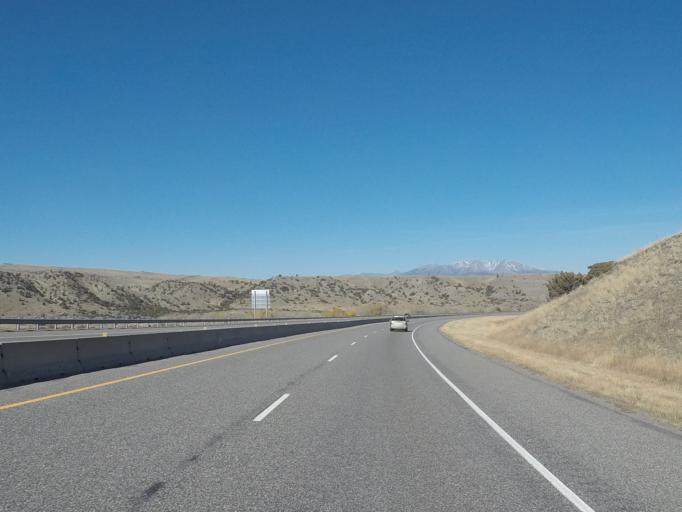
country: US
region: Montana
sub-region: Park County
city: Livingston
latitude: 45.7104
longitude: -110.2632
